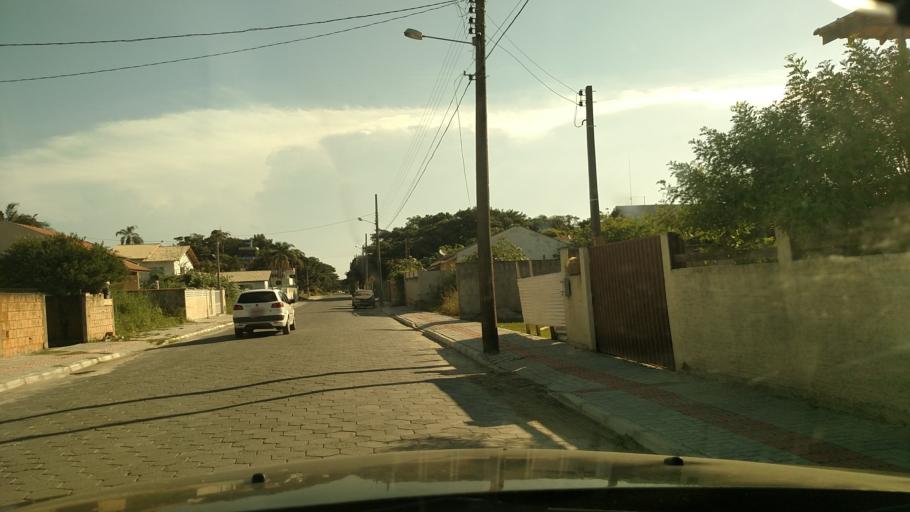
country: BR
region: Santa Catarina
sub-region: Porto Belo
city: Porto Belo
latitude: -27.1792
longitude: -48.5079
